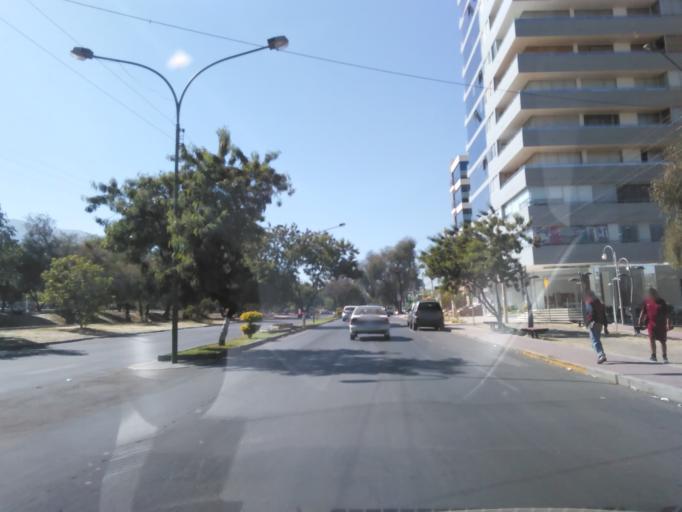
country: BO
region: Cochabamba
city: Cochabamba
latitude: -17.3736
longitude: -66.1459
